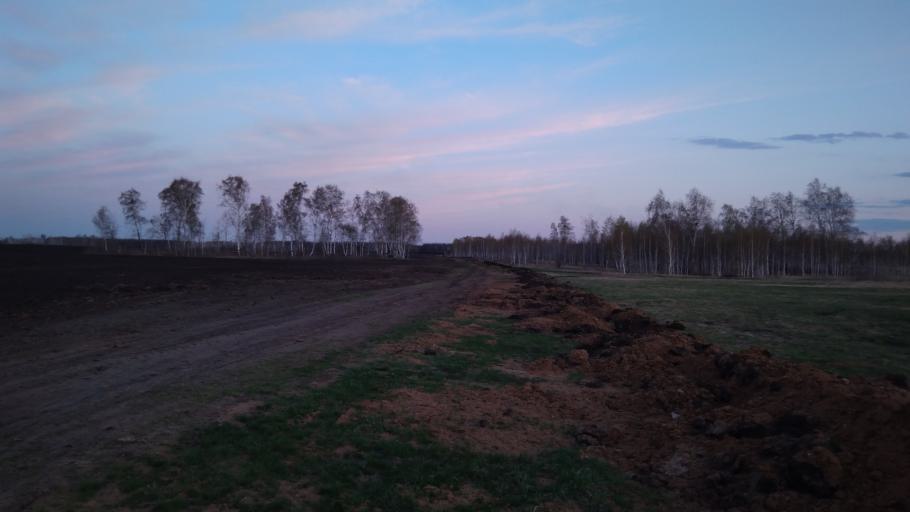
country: RU
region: Chelyabinsk
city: Bobrovka
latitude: 54.0840
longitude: 61.6812
